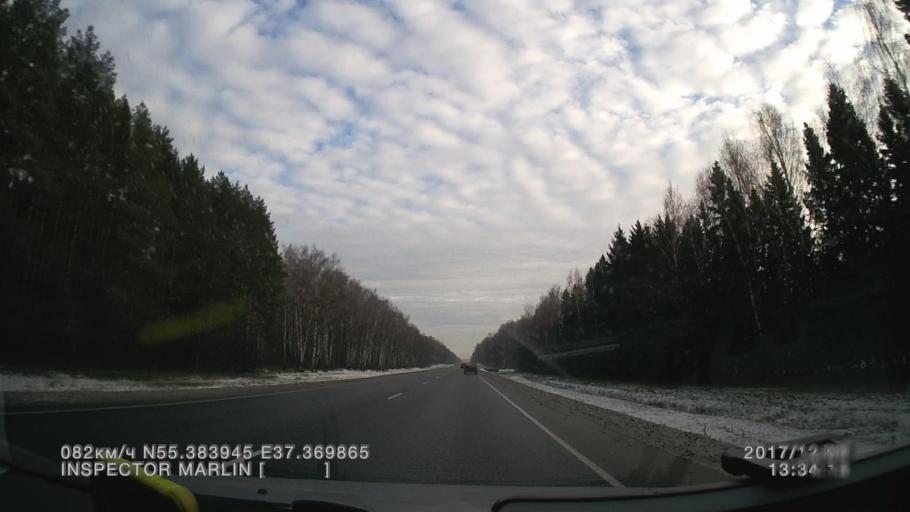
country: RU
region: Moskovskaya
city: Troitsk
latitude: 55.3839
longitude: 37.3700
